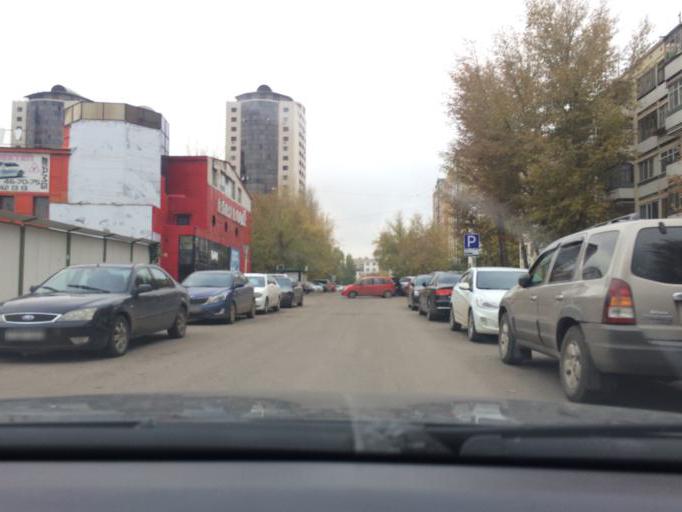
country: KZ
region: Astana Qalasy
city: Astana
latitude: 51.1643
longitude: 71.4381
